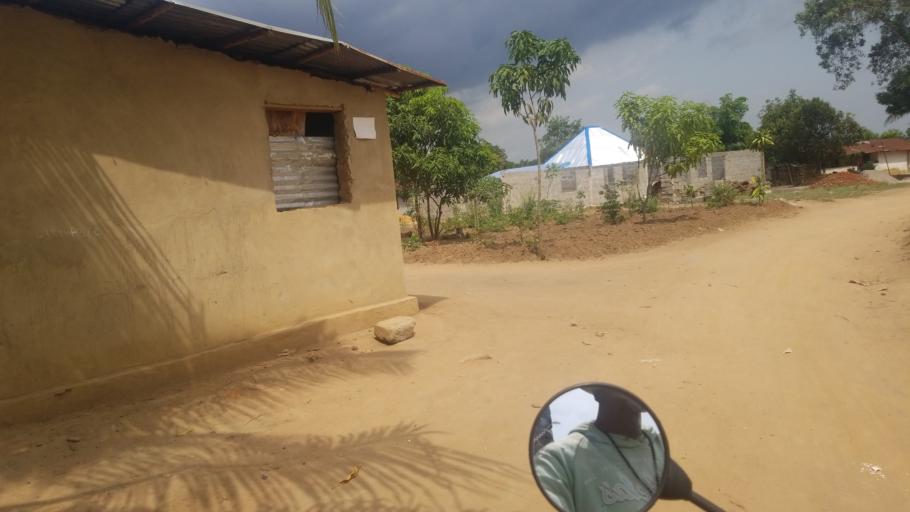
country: SL
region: Western Area
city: Waterloo
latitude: 8.3141
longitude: -13.0483
